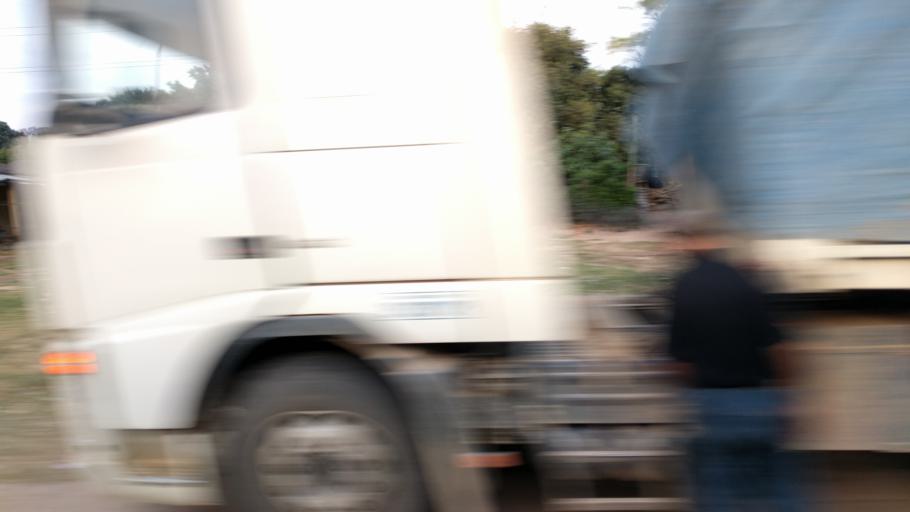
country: BO
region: Santa Cruz
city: Santa Rita
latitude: -17.9565
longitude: -63.3585
